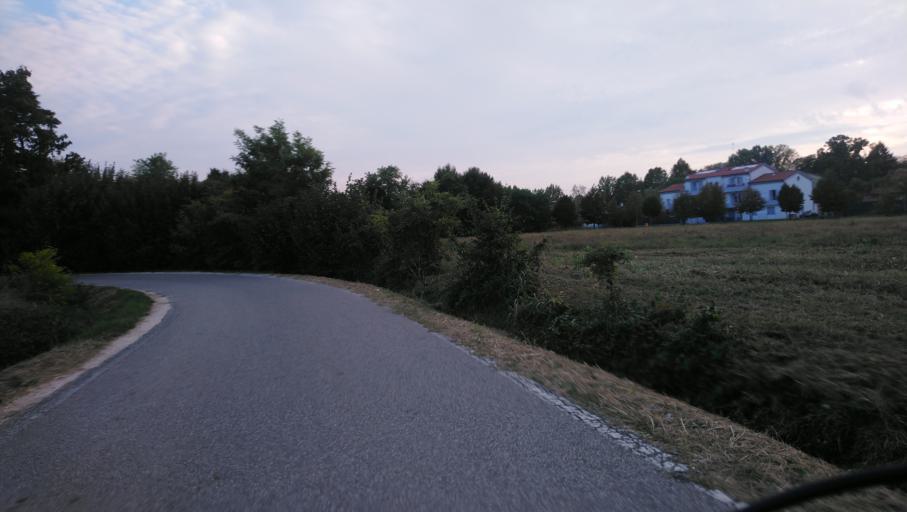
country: IT
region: Veneto
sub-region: Provincia di Treviso
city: Treviso
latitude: 45.6915
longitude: 12.2367
